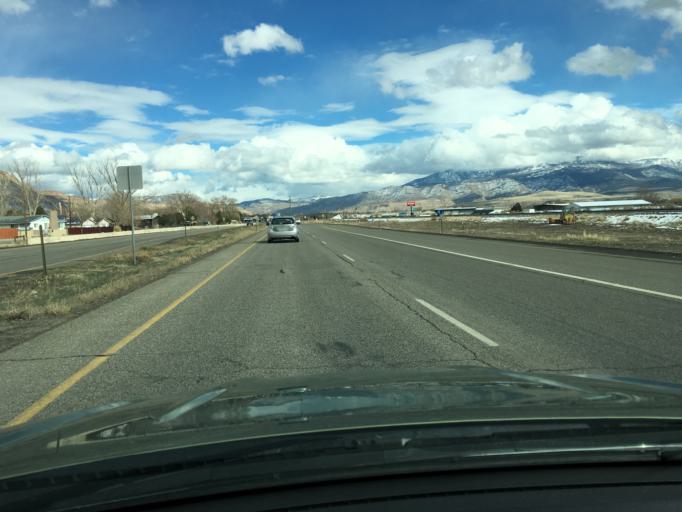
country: US
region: Colorado
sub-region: Mesa County
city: Clifton
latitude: 39.0840
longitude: -108.4683
